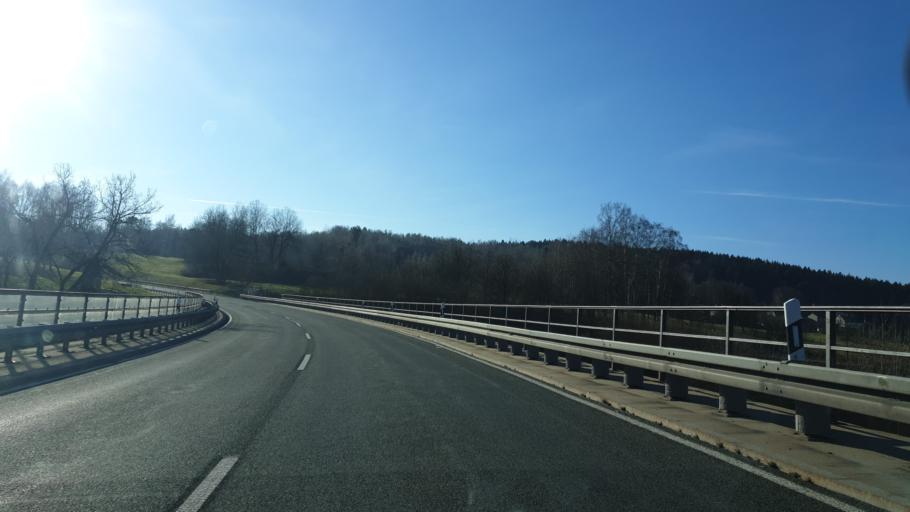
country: DE
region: Saxony
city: Bad Brambach
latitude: 50.2202
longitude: 12.3185
